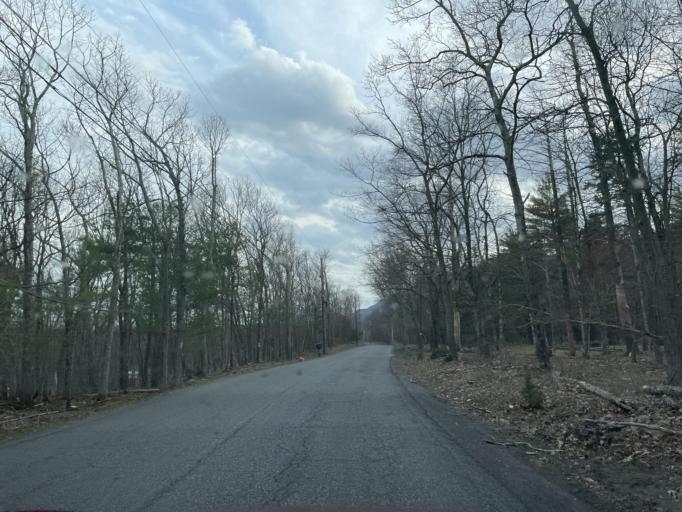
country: US
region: New York
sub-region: Ulster County
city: Manorville
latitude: 42.1240
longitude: -74.0435
